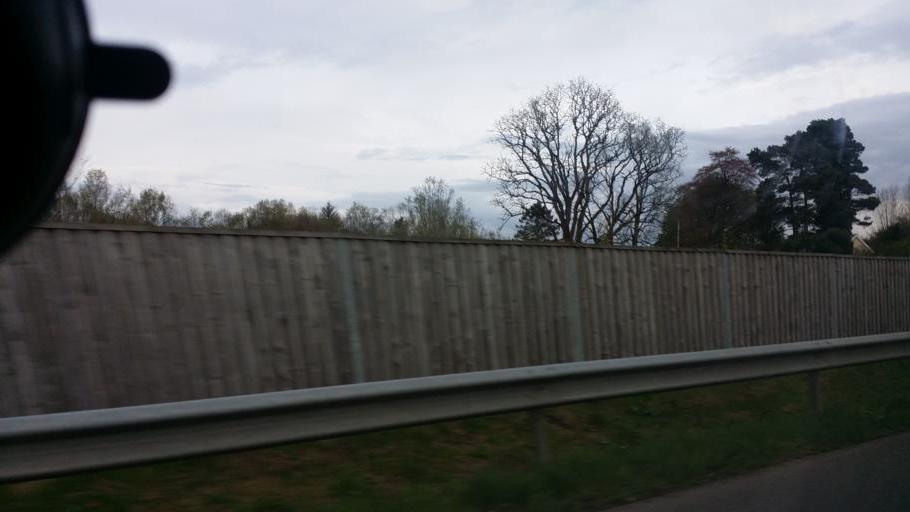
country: IE
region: Ulster
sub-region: An Cabhan
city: Belturbet
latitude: 54.0685
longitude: -7.4055
